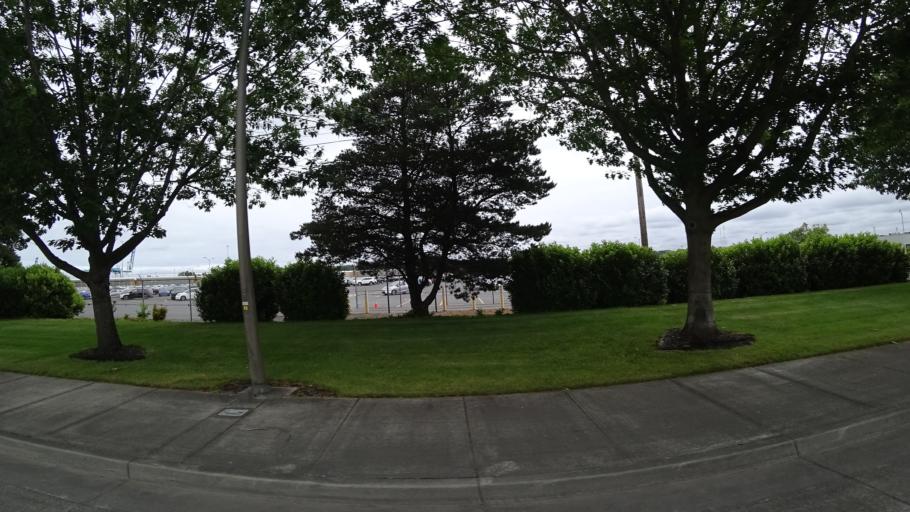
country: US
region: Washington
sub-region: Clark County
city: Lake Shore
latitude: 45.6289
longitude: -122.7425
